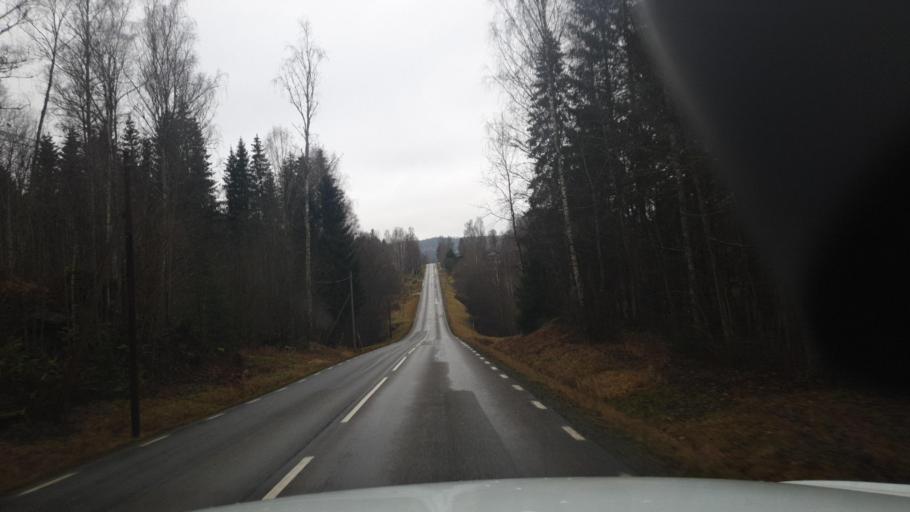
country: SE
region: Vaermland
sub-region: Eda Kommun
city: Amotfors
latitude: 59.6657
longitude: 12.4241
